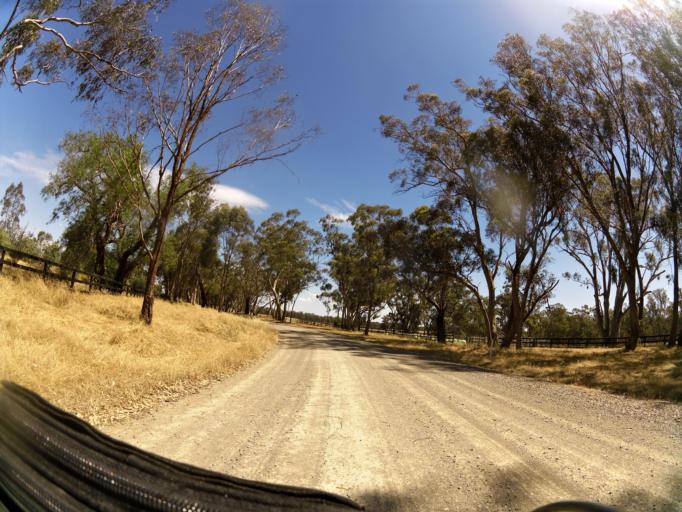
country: AU
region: Victoria
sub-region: Campaspe
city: Kyabram
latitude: -36.8315
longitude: 145.0745
